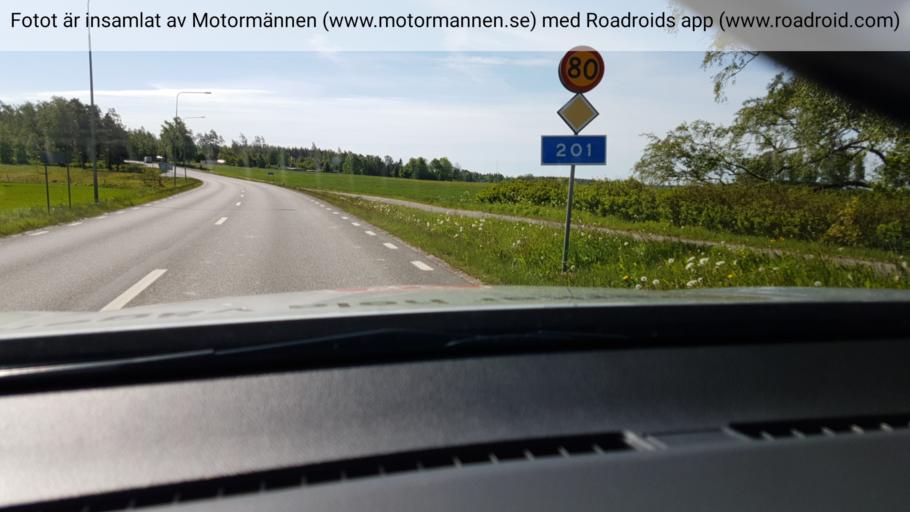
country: SE
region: Vaestra Goetaland
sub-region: Tibro Kommun
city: Tibro
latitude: 58.4072
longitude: 14.1861
